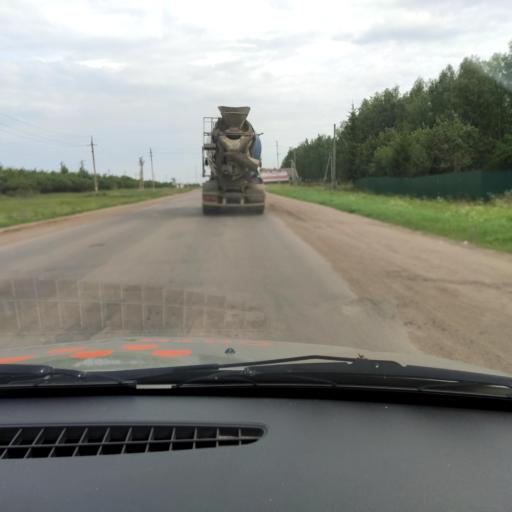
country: RU
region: Bashkortostan
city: Iglino
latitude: 54.8560
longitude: 56.4554
